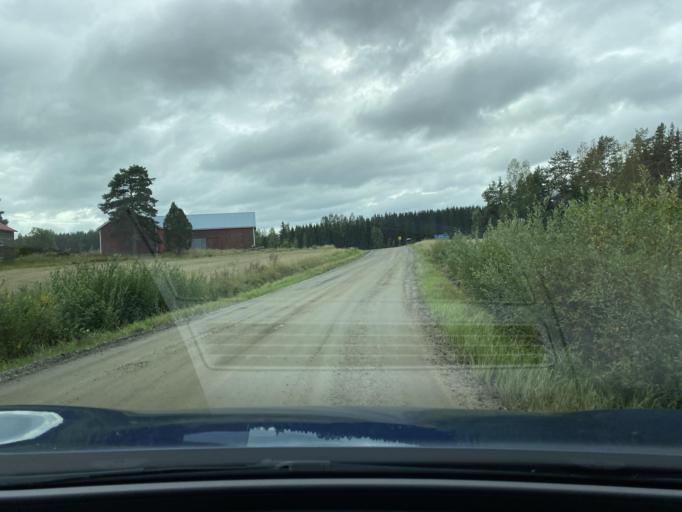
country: FI
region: Pirkanmaa
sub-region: Lounais-Pirkanmaa
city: Punkalaidun
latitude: 61.1714
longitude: 23.1805
